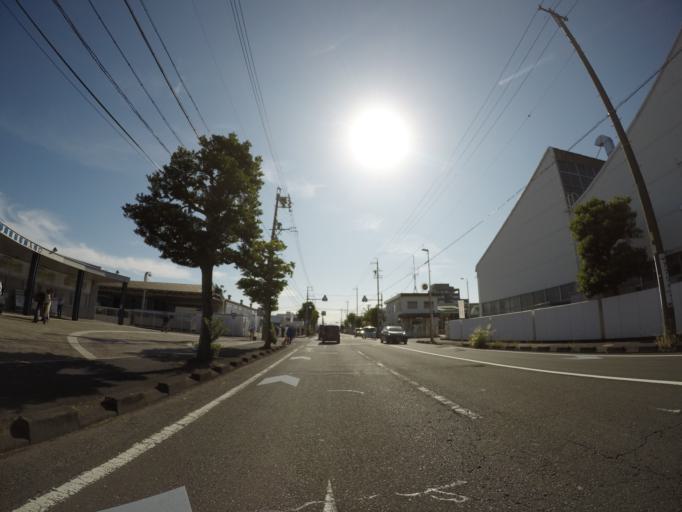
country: JP
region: Shizuoka
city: Shizuoka-shi
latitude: 34.9715
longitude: 138.4188
